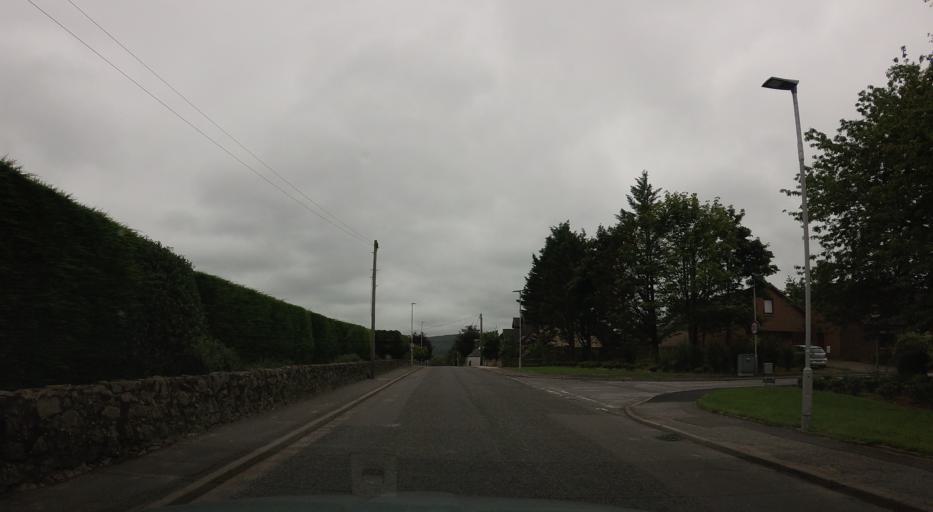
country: GB
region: Scotland
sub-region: Aberdeenshire
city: Banchory
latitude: 57.0593
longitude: -2.4930
